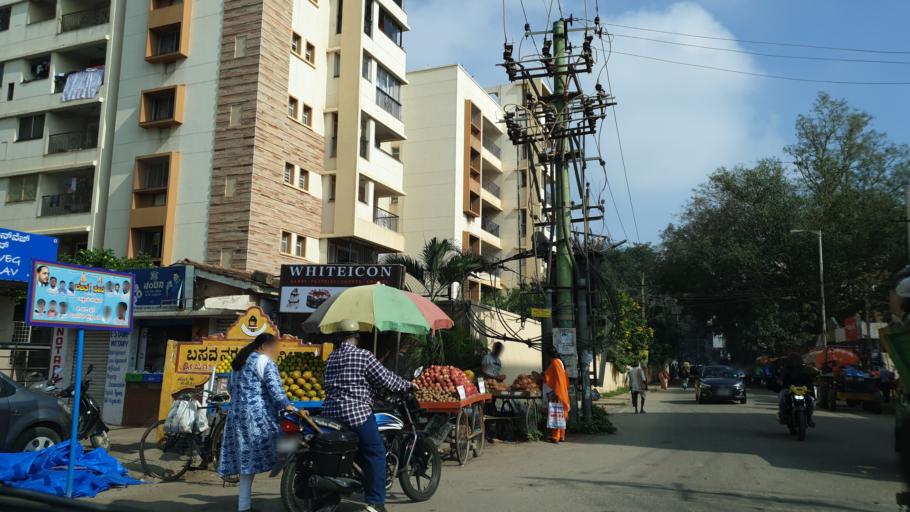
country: IN
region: Karnataka
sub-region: Bangalore Urban
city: Bangalore
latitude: 12.9671
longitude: 77.6826
